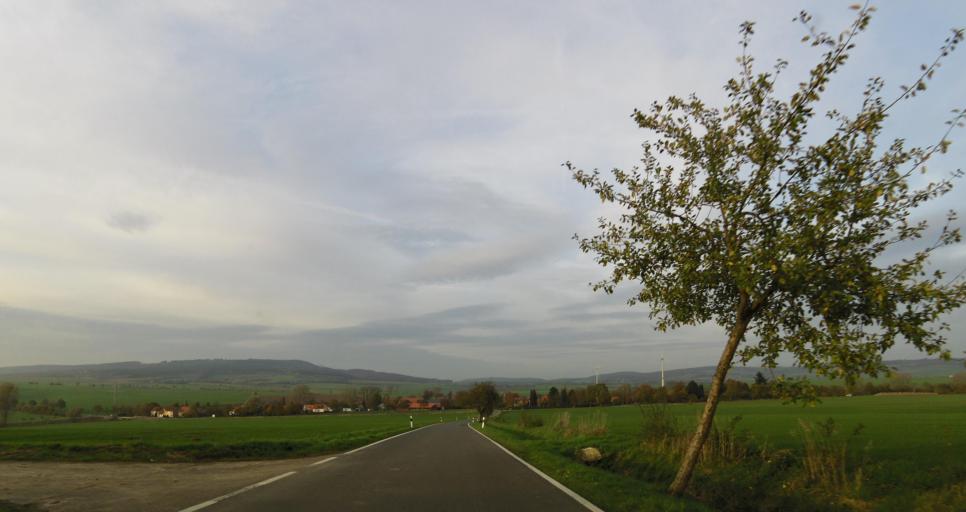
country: DE
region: Lower Saxony
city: Einbeck
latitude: 51.8593
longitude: 9.8597
